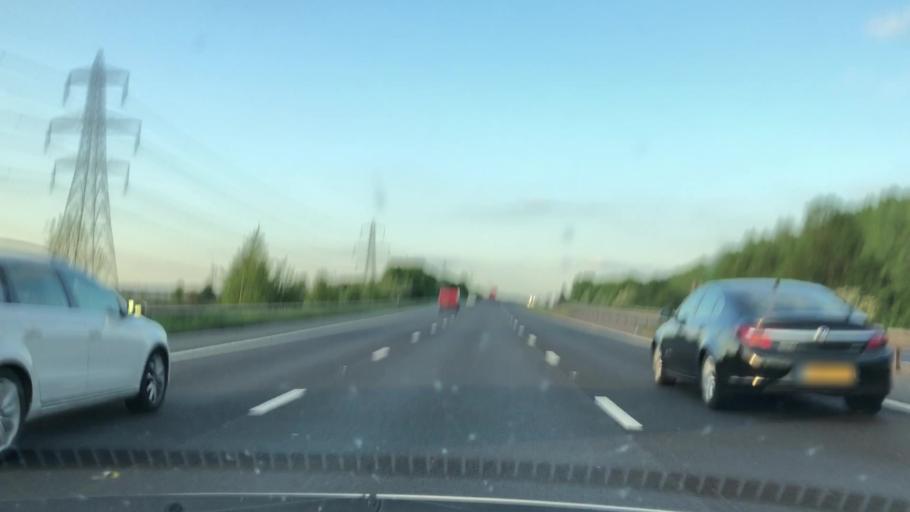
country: GB
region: England
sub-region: Cheshire West and Chester
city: Helsby
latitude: 53.2724
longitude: -2.7882
